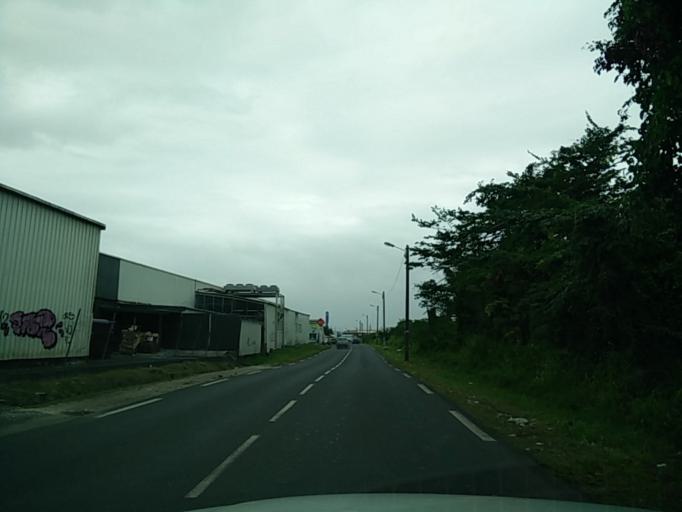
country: GP
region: Guadeloupe
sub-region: Guadeloupe
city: Baie-Mahault
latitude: 16.2534
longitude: -61.5653
